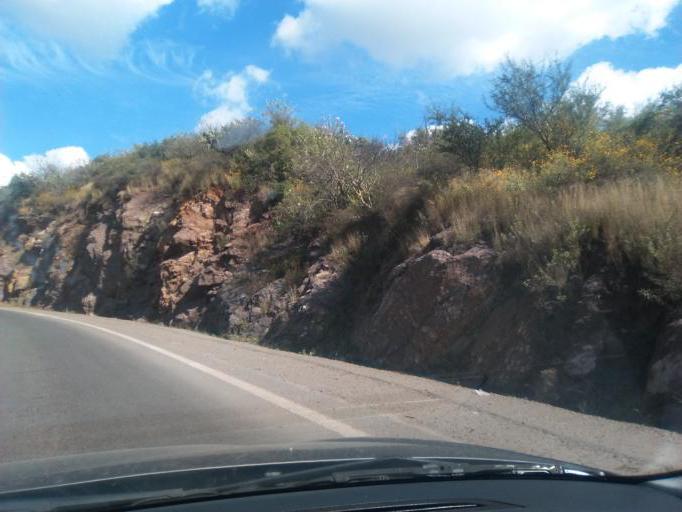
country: MX
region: Guanajuato
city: Marfil
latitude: 20.9996
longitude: -101.2725
